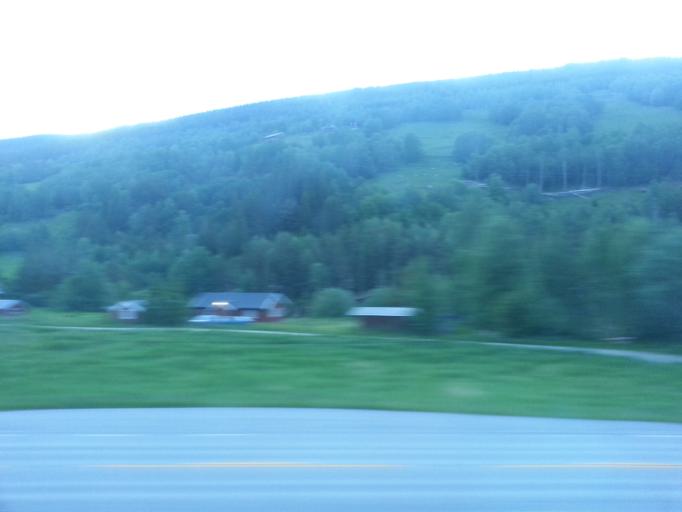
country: NO
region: Oppland
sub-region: Dovre
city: Dovre
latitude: 61.8981
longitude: 9.3851
